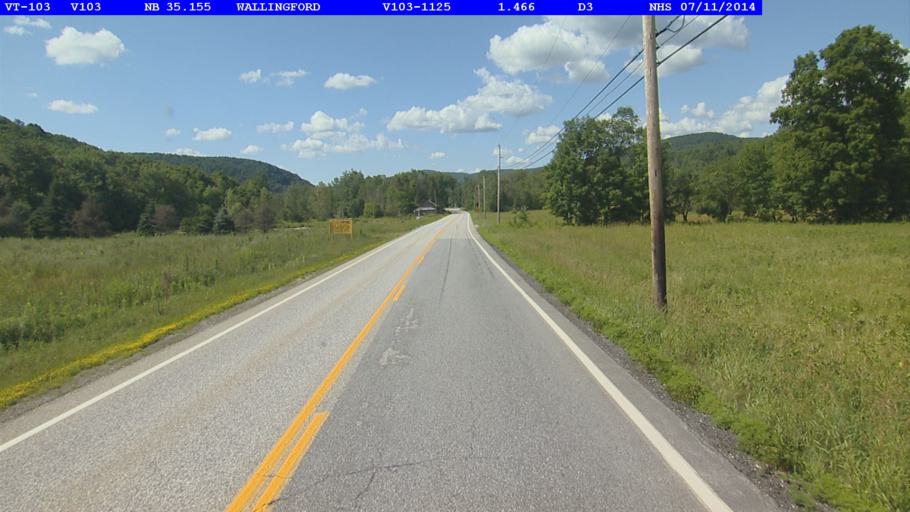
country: US
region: Vermont
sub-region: Rutland County
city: Rutland
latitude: 43.4709
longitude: -72.8740
